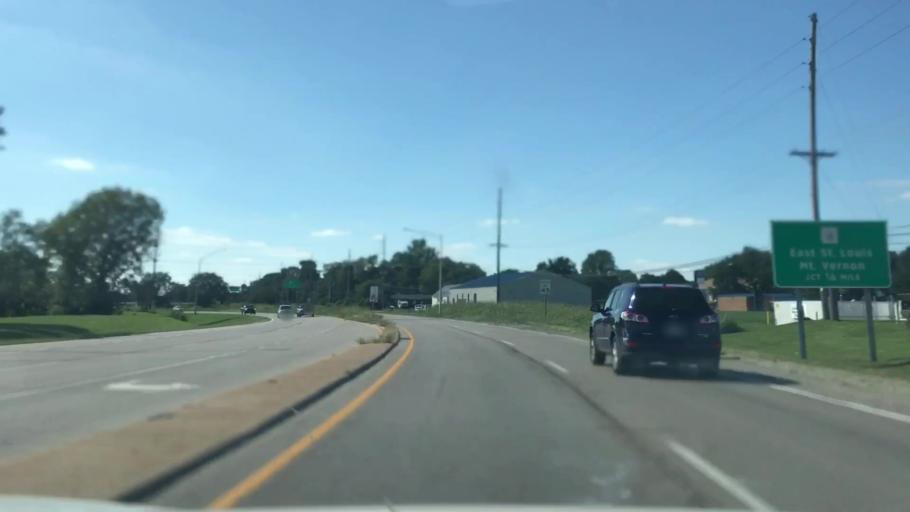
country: US
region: Illinois
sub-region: Saint Clair County
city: Swansea
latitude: 38.5473
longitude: -90.0551
